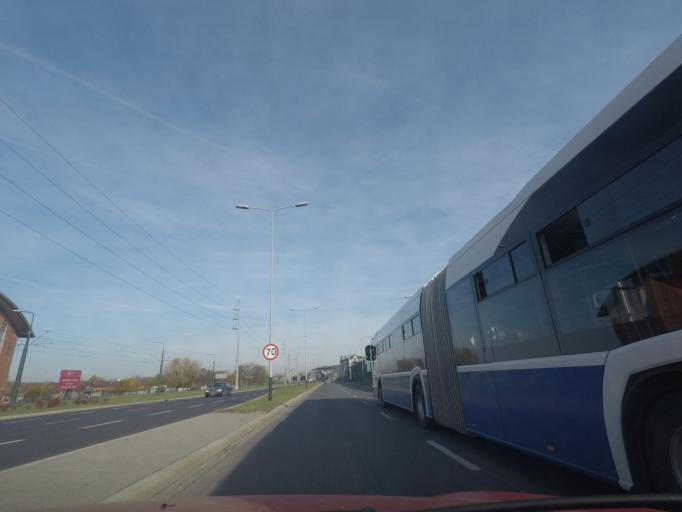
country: PL
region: Lesser Poland Voivodeship
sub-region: Krakow
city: Sidzina
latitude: 50.0210
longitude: 19.8989
